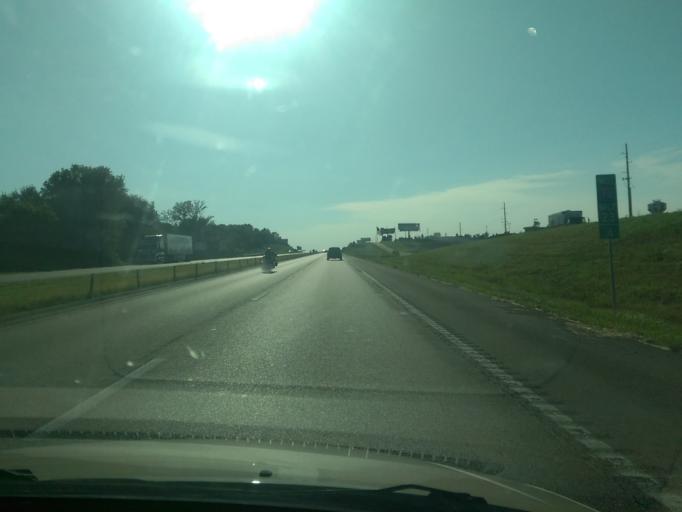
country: US
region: Missouri
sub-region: Jackson County
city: Grain Valley
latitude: 39.0233
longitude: -94.2128
